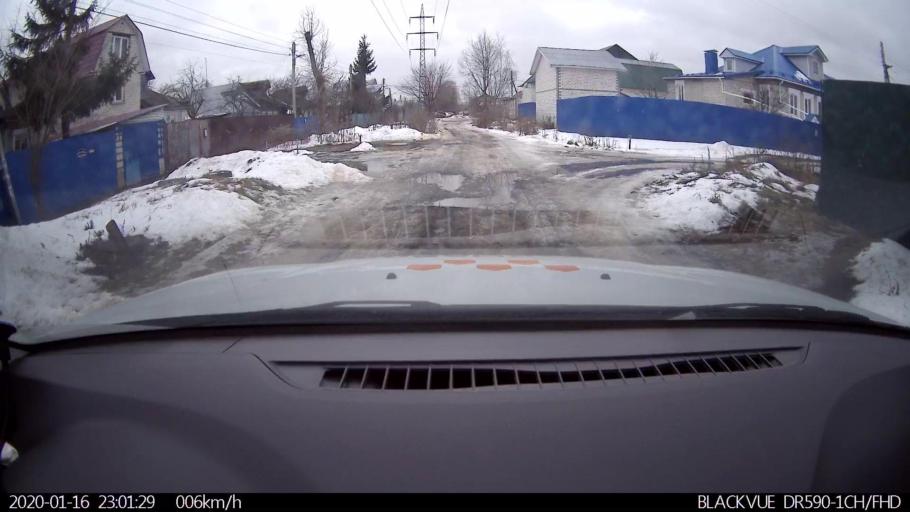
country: RU
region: Nizjnij Novgorod
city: Nizhniy Novgorod
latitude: 56.2849
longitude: 43.9046
